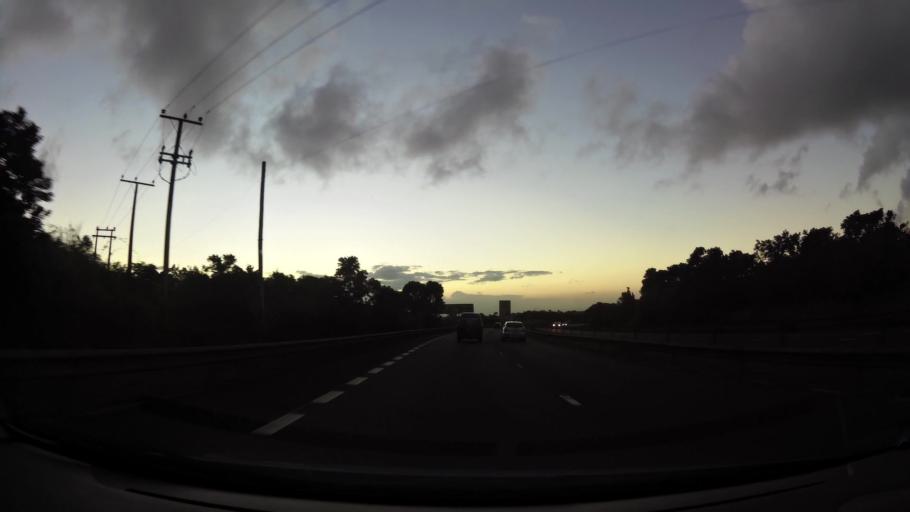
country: MU
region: Plaines Wilhems
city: Curepipe
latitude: -20.2934
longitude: 57.5279
